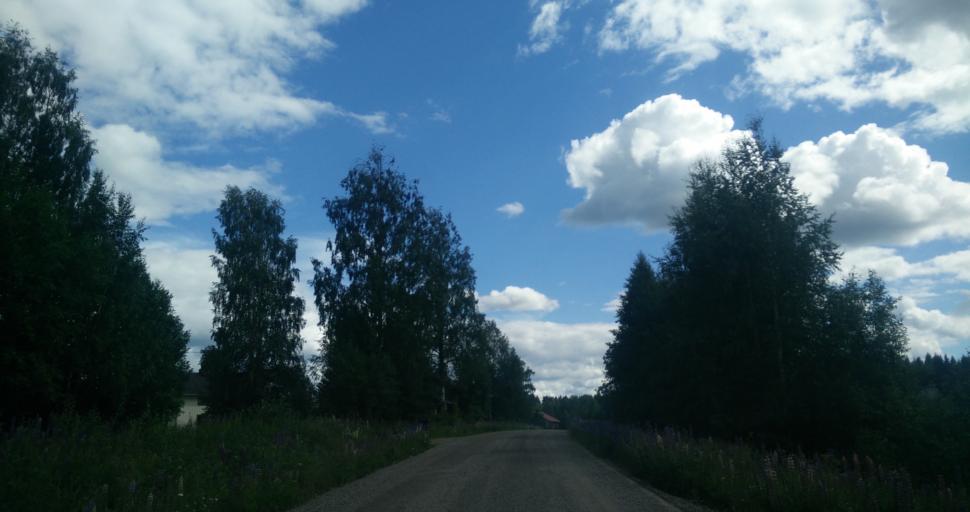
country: SE
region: Gaevleborg
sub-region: Nordanstigs Kommun
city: Bergsjoe
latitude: 62.0691
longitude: 16.7697
